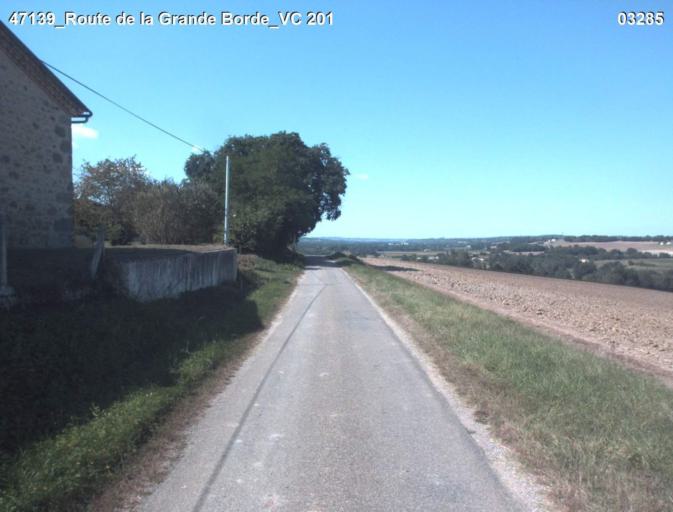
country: FR
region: Aquitaine
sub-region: Departement du Lot-et-Garonne
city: Nerac
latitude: 44.0883
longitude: 0.3806
